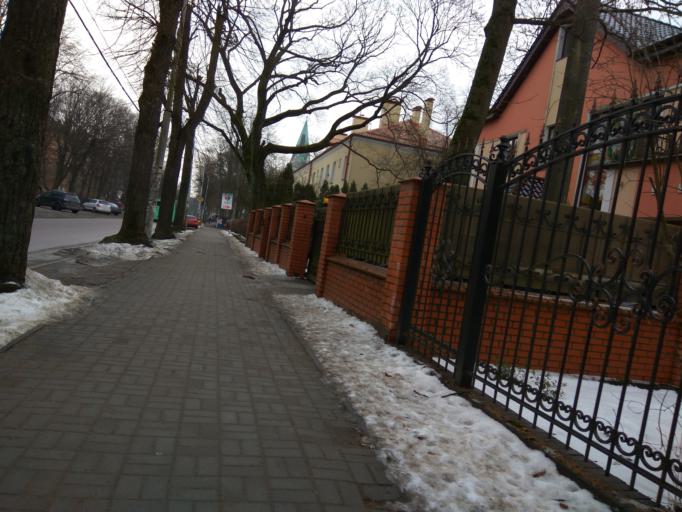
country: RU
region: Kaliningrad
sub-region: Gorod Kaliningrad
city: Kaliningrad
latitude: 54.7182
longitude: 20.4720
